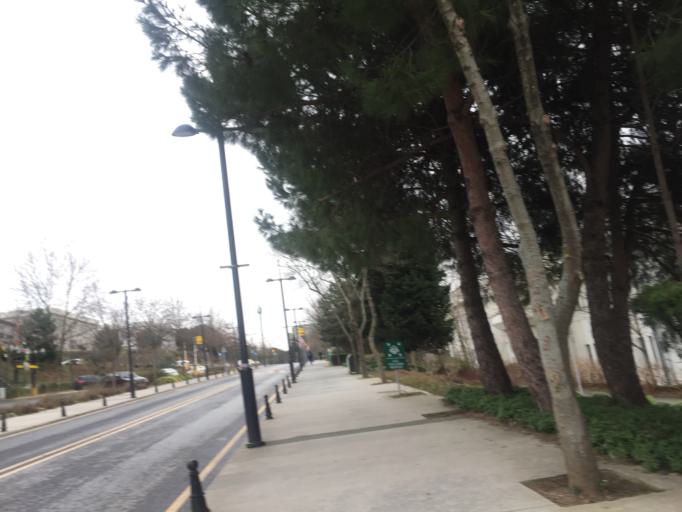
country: TR
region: Istanbul
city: Sisli
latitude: 41.1050
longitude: 29.0246
